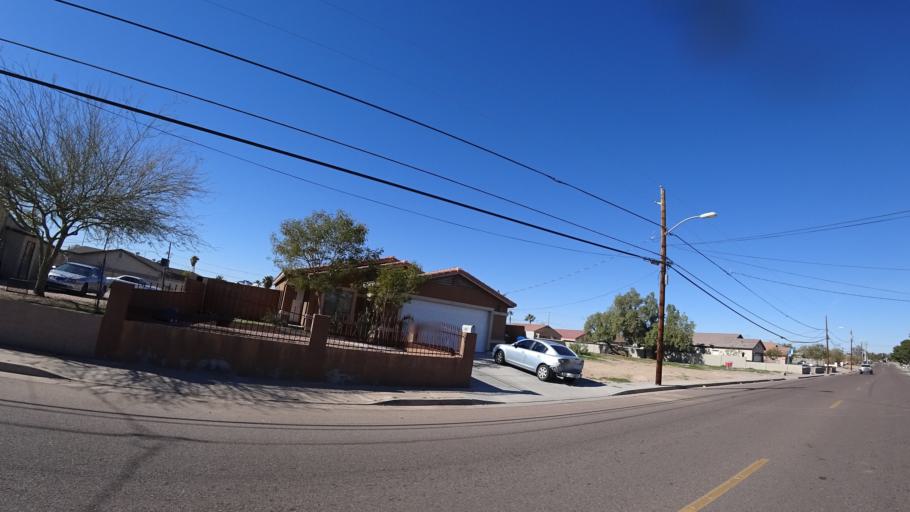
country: US
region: Arizona
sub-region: Maricopa County
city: Avondale
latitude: 33.4283
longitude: -112.3451
